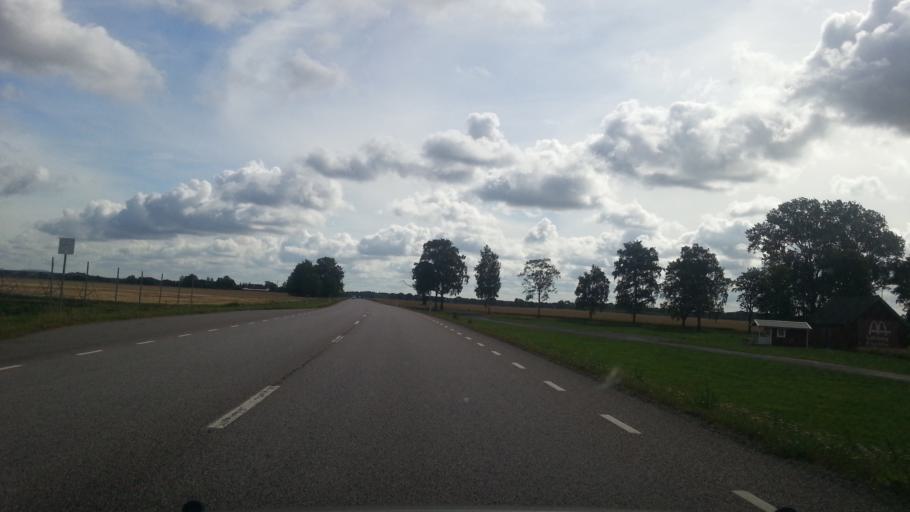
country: SE
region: Vaestra Goetaland
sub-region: Lidkopings Kommun
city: Lidkoping
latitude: 58.4802
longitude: 13.0918
